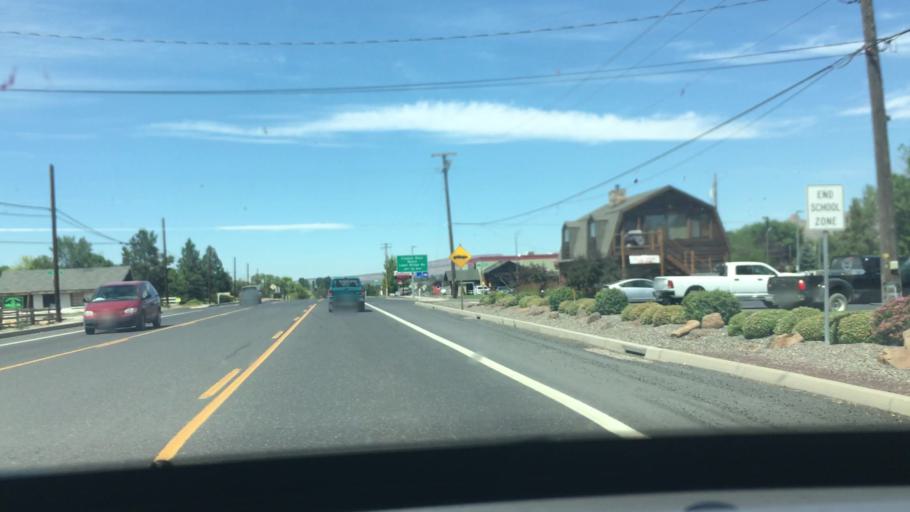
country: US
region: Oregon
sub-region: Deschutes County
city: Terrebonne
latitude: 44.3520
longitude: -121.1788
